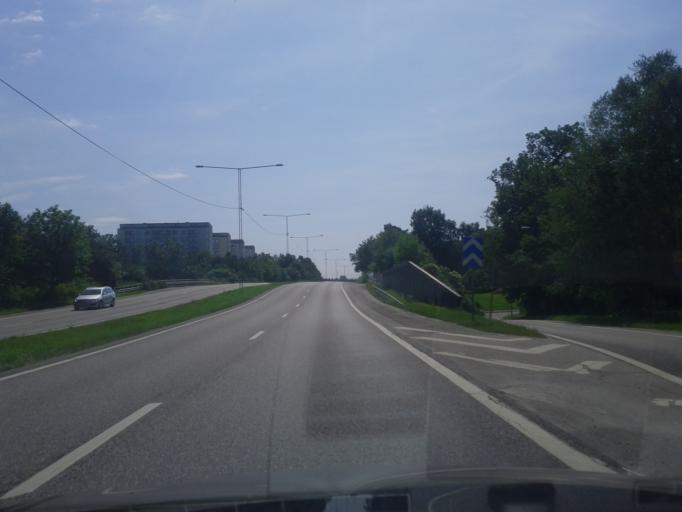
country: SE
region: Stockholm
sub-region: Huddinge Kommun
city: Huddinge
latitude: 59.2648
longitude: 18.0063
